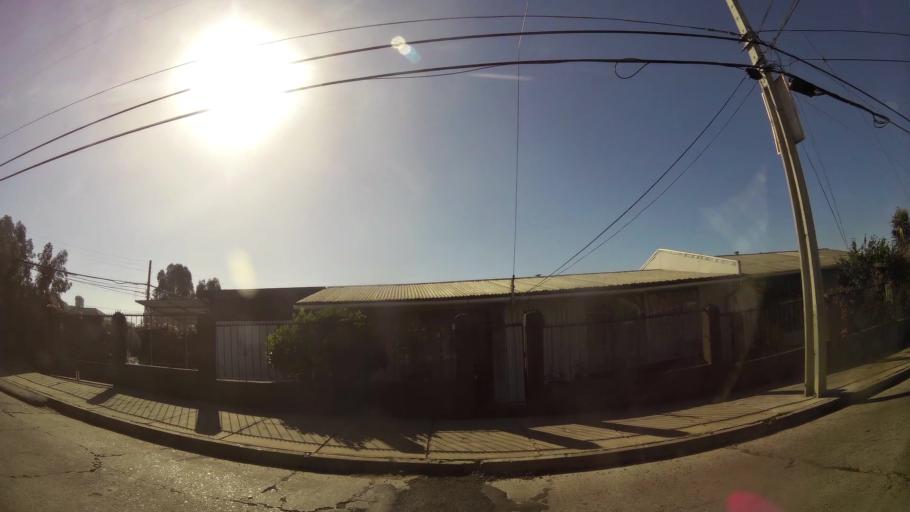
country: CL
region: Valparaiso
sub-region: Provincia de Valparaiso
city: Vina del Mar
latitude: -33.0322
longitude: -71.5584
